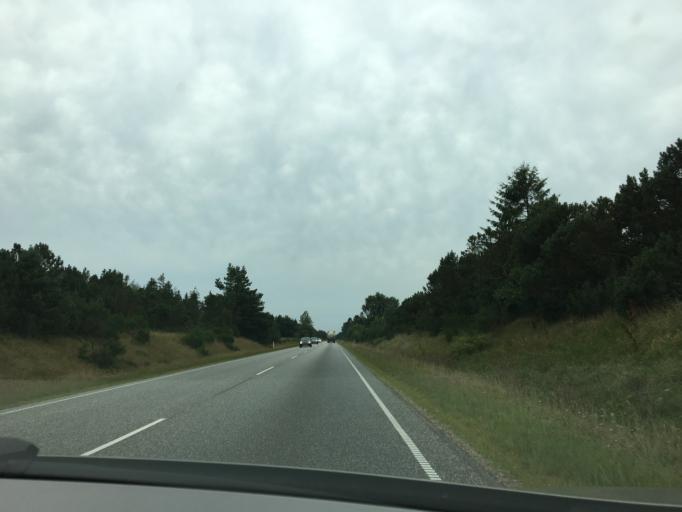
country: DK
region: Central Jutland
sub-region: Herning Kommune
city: Sunds
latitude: 56.3766
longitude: 8.9859
